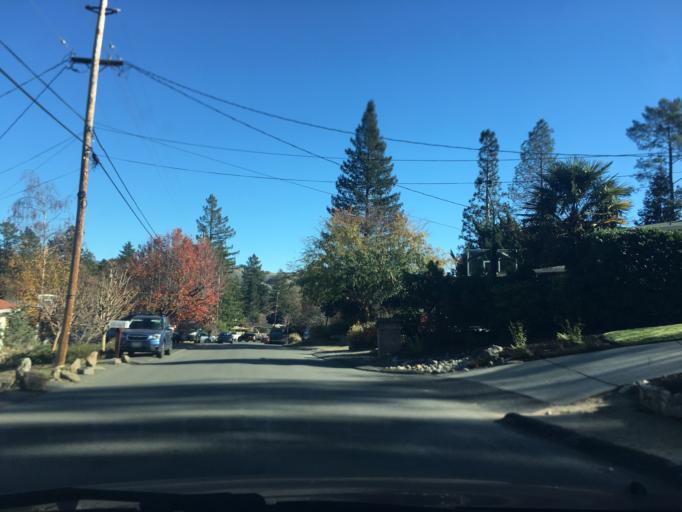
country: US
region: California
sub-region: Contra Costa County
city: Lafayette
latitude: 37.8739
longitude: -122.1034
